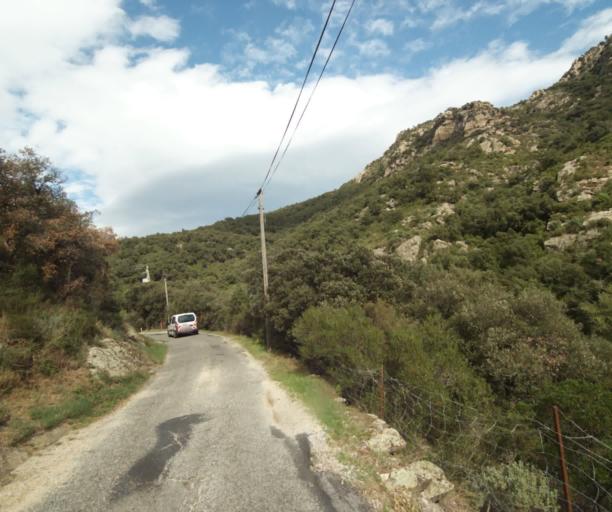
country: FR
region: Languedoc-Roussillon
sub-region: Departement des Pyrenees-Orientales
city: Sorede
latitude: 42.5209
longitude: 2.9902
